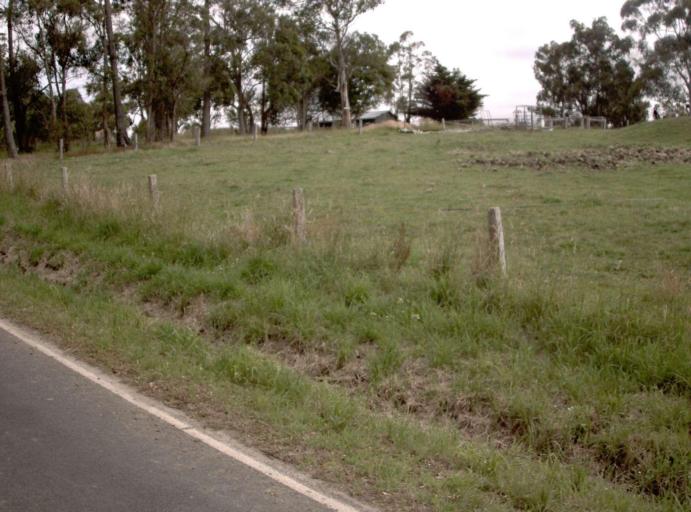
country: AU
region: Victoria
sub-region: Latrobe
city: Traralgon
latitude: -38.3822
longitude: 146.7949
